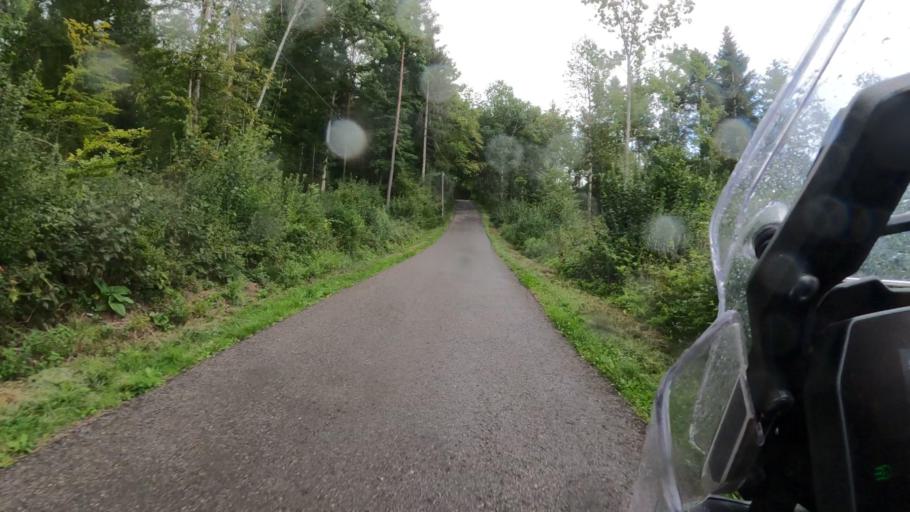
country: DE
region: Baden-Wuerttemberg
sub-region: Freiburg Region
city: Eggingen
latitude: 47.6713
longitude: 8.3993
